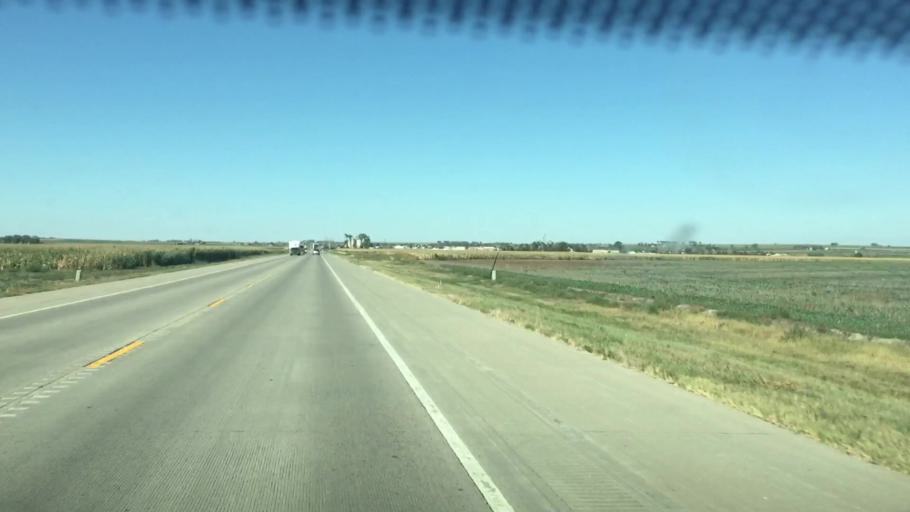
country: US
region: Colorado
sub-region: Prowers County
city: Lamar
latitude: 38.1324
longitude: -102.7237
